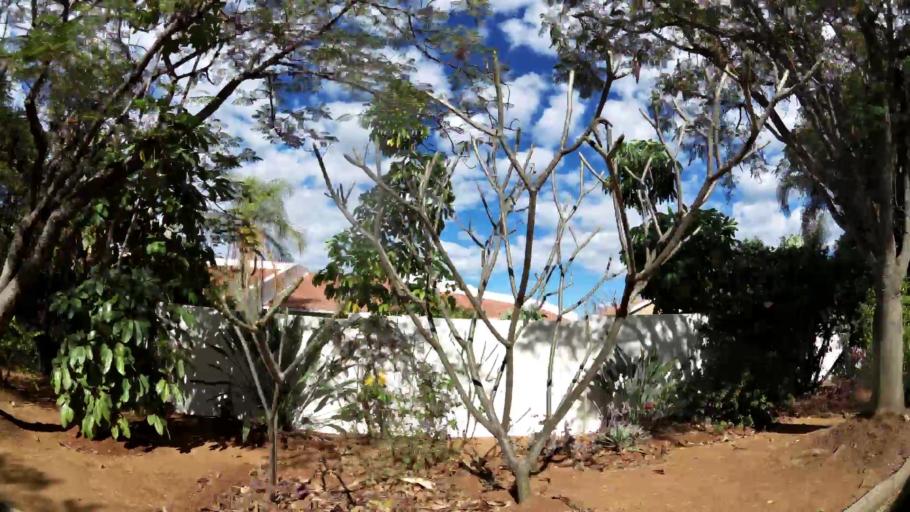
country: ZA
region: Limpopo
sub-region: Waterberg District Municipality
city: Warmbaths
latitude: -24.8756
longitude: 28.2874
